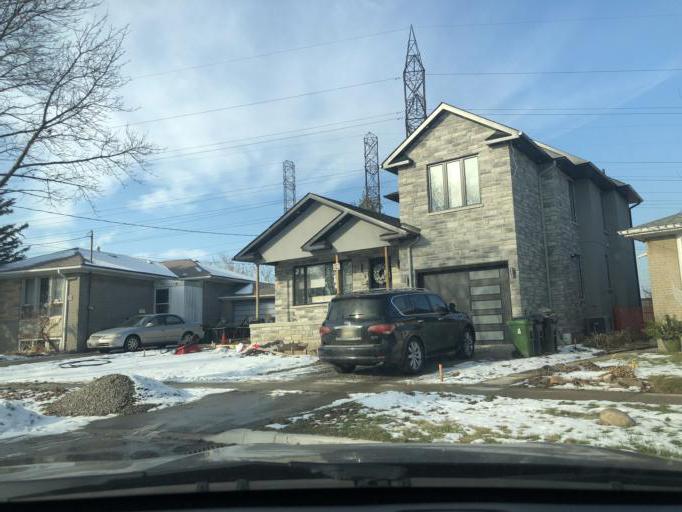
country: CA
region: Ontario
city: Etobicoke
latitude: 43.6669
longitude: -79.5844
